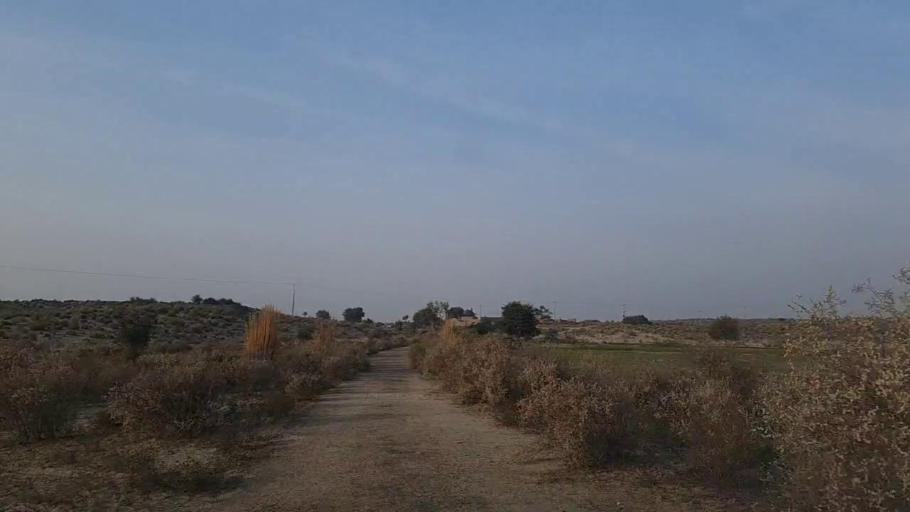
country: PK
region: Sindh
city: Jam Sahib
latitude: 26.4316
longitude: 68.6036
